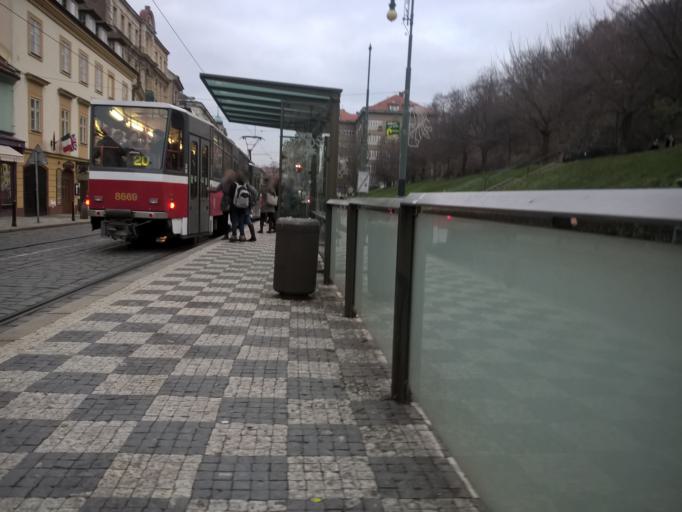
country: CZ
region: Praha
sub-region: Praha 1
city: Mala Strana
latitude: 50.0821
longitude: 14.4044
